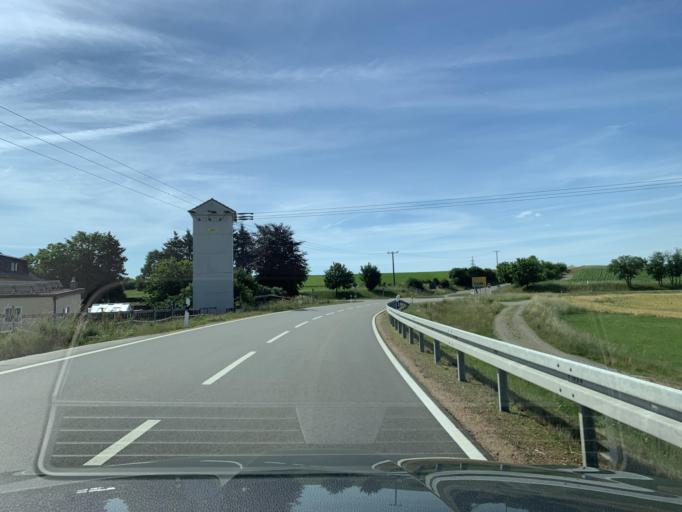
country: DE
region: Bavaria
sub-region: Upper Palatinate
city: Pettendorf
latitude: 49.3409
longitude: 12.3324
